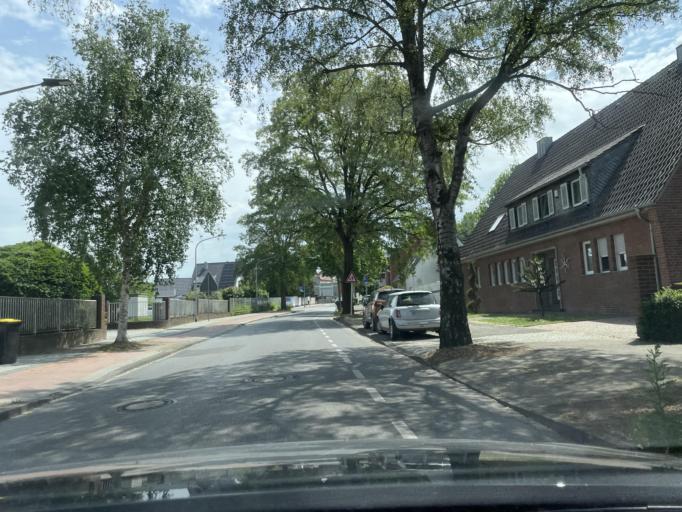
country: DE
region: North Rhine-Westphalia
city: Wegberg
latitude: 51.1482
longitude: 6.3650
